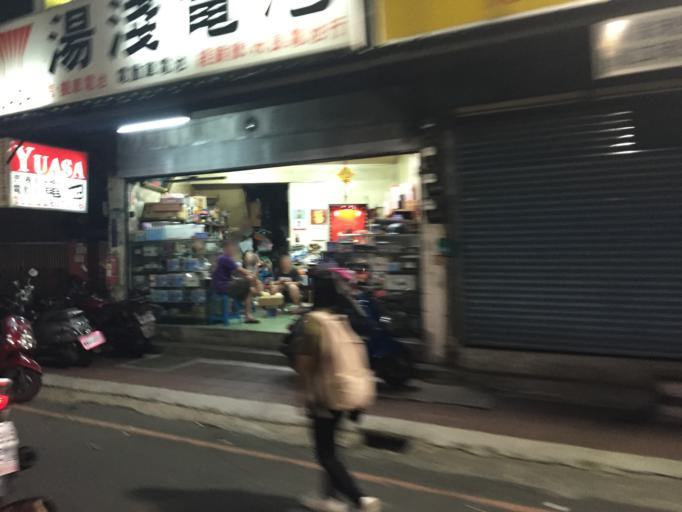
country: TW
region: Taipei
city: Taipei
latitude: 25.0851
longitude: 121.4715
